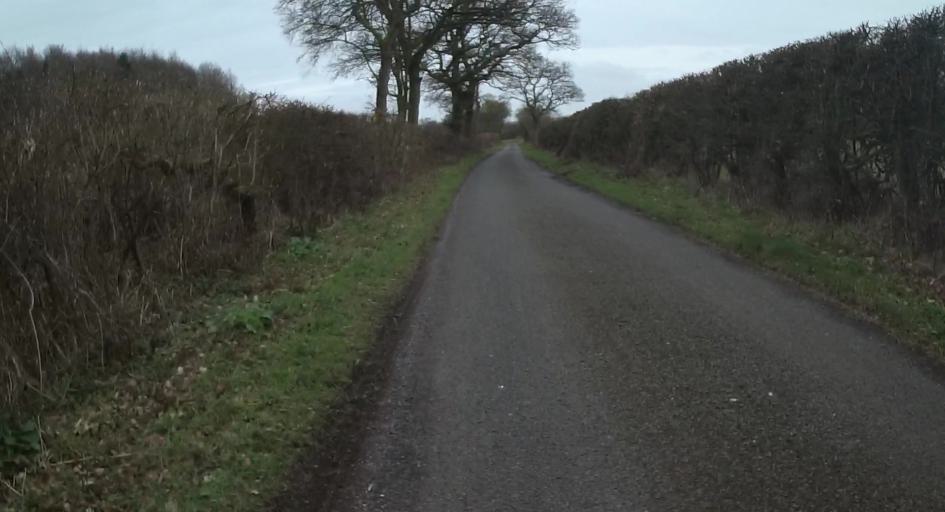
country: GB
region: England
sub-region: Hampshire
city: Overton
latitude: 51.2653
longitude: -1.2462
